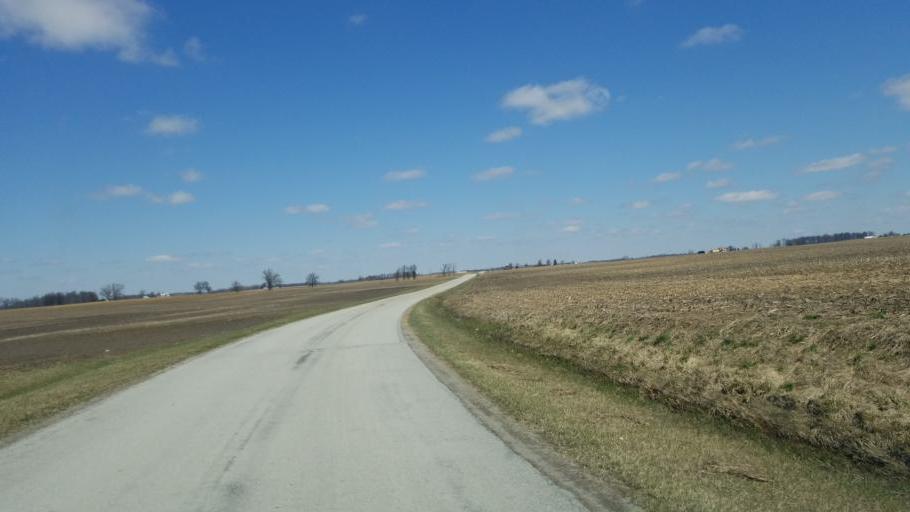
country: US
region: Ohio
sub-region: Wyandot County
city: Upper Sandusky
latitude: 40.7257
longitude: -83.1880
